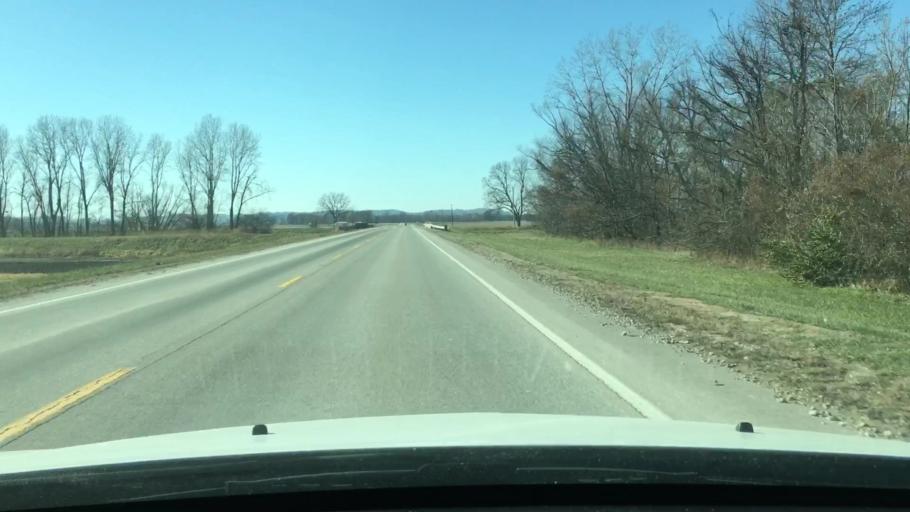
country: US
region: Missouri
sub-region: Pike County
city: Louisiana
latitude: 39.5048
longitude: -90.9874
